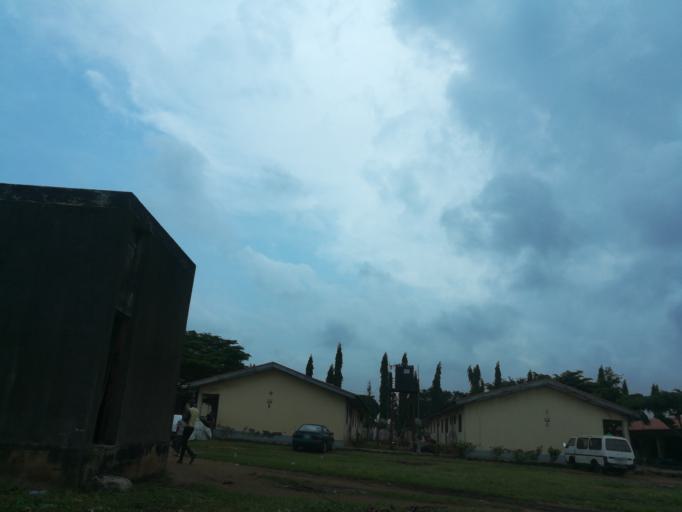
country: NG
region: Lagos
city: Oshodi
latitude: 6.5658
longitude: 3.3511
